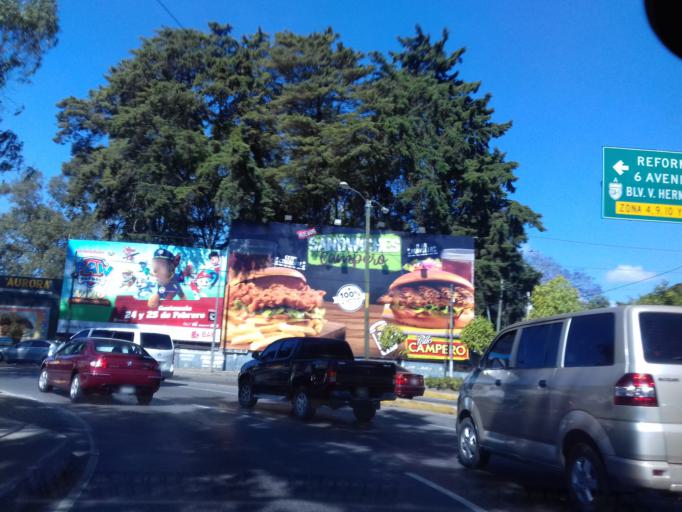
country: GT
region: Guatemala
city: Guatemala City
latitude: 14.6167
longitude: -90.5084
